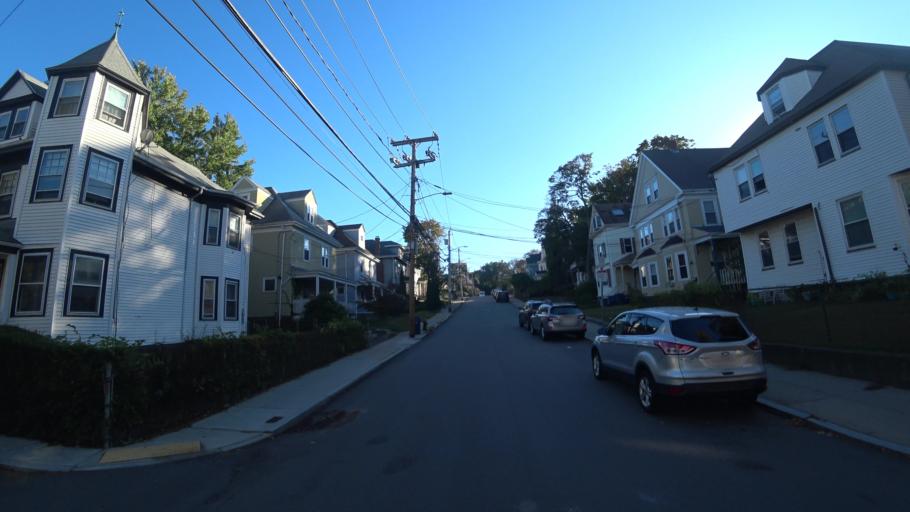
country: US
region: Massachusetts
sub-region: Norfolk County
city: Brookline
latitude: 42.3523
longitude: -71.1467
